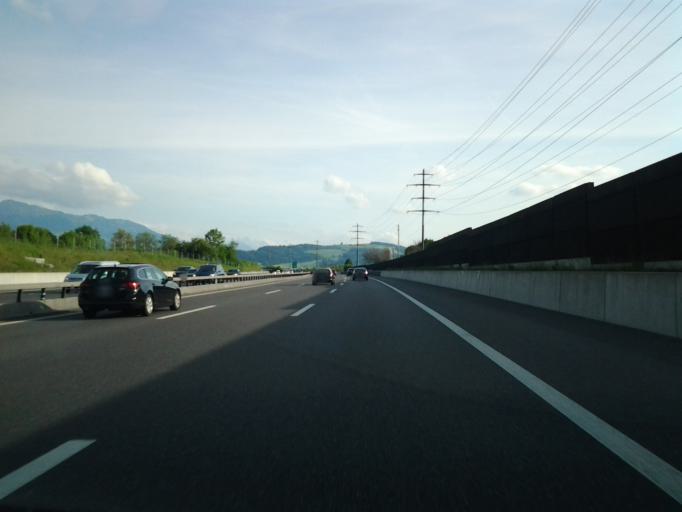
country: CH
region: Zug
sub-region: Zug
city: Hunenberg
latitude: 47.1762
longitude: 8.4326
